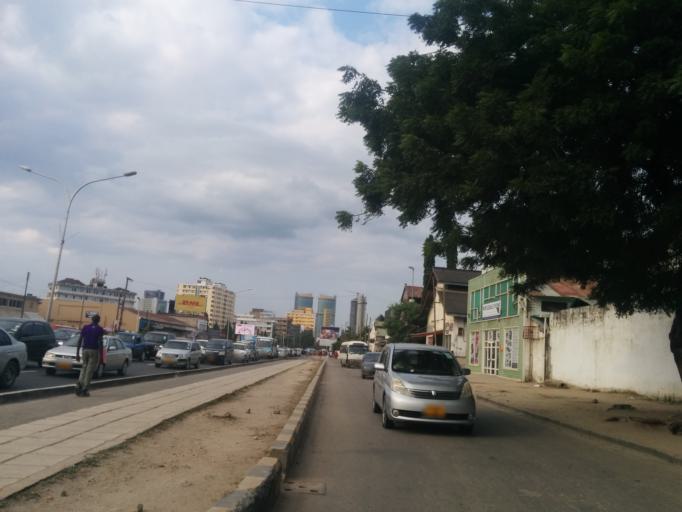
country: TZ
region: Dar es Salaam
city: Dar es Salaam
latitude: -6.8288
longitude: 39.2746
